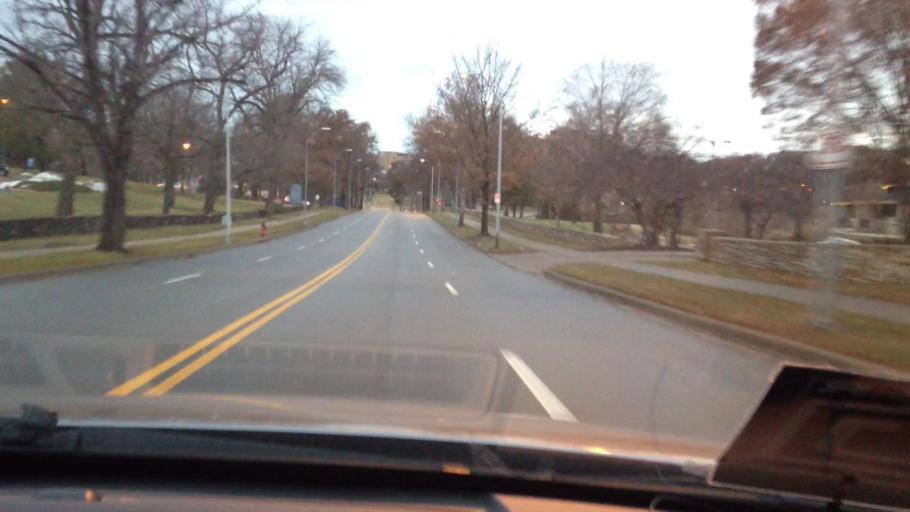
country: US
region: Kansas
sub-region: Johnson County
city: Westwood
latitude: 39.0367
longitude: -94.5761
